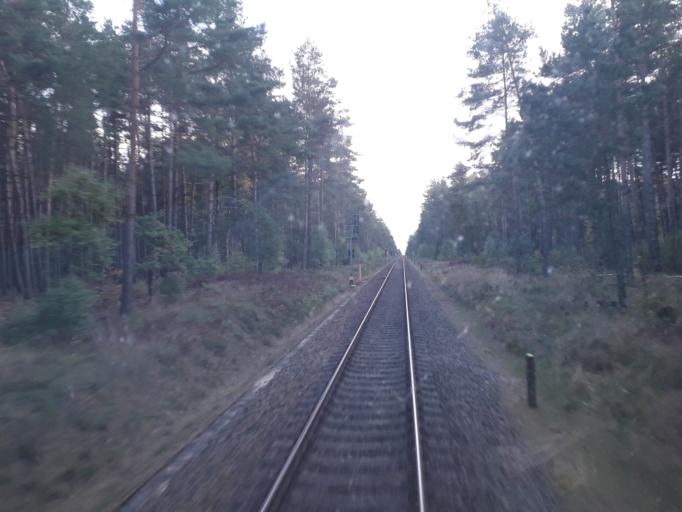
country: DE
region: Brandenburg
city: Wittstock
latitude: 53.1052
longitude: 12.5327
